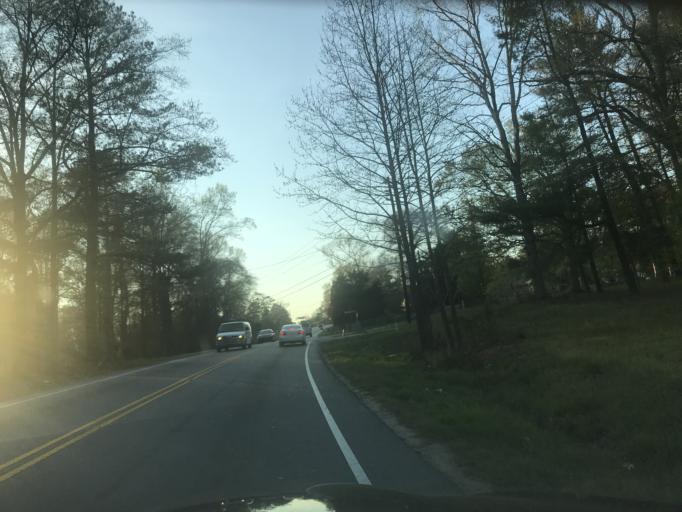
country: US
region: North Carolina
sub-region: Wake County
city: Knightdale
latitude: 35.7591
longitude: -78.5499
